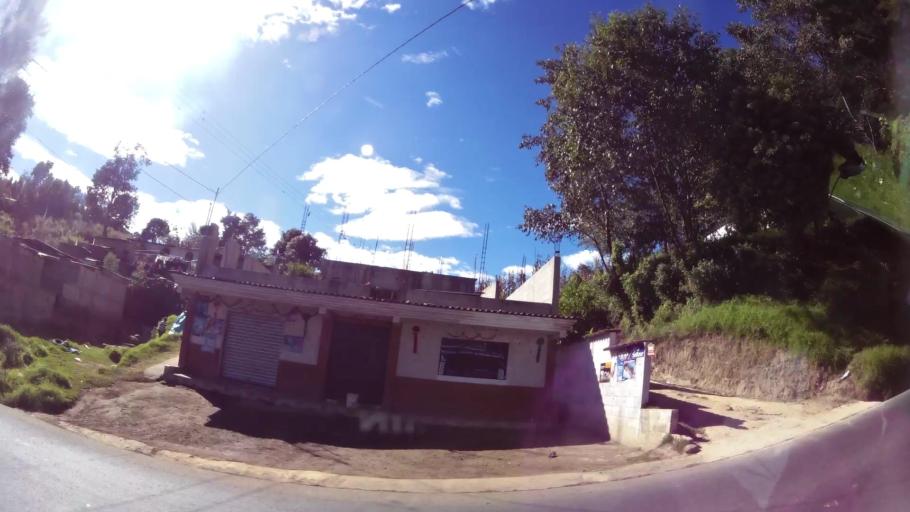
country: GT
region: Solola
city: Solola
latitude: 14.7856
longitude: -91.1829
